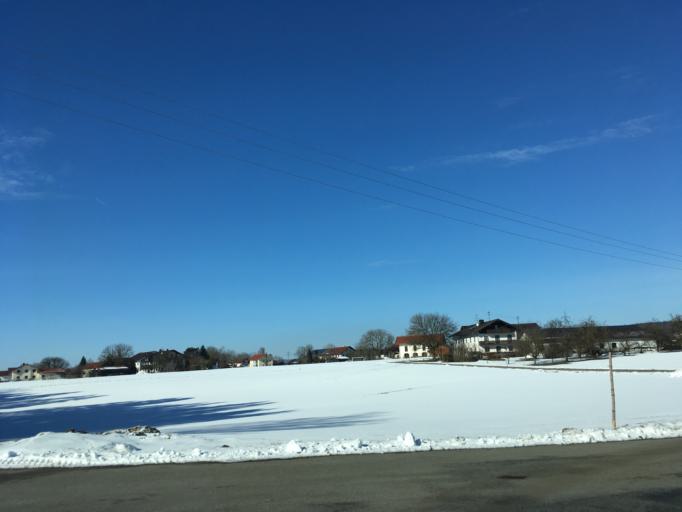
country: DE
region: Bavaria
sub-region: Upper Bavaria
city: Rechtmehring
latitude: 48.1098
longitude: 12.1548
